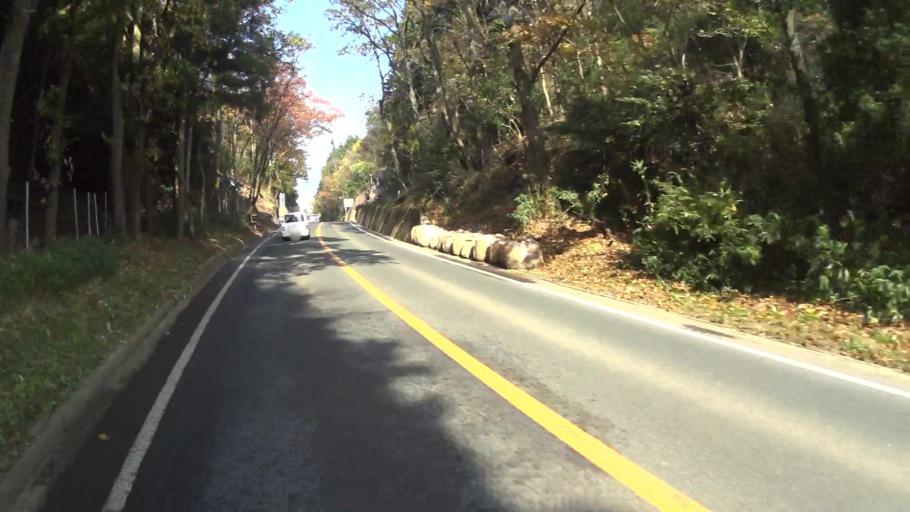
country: JP
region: Kyoto
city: Fukuchiyama
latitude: 35.2628
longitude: 135.1463
